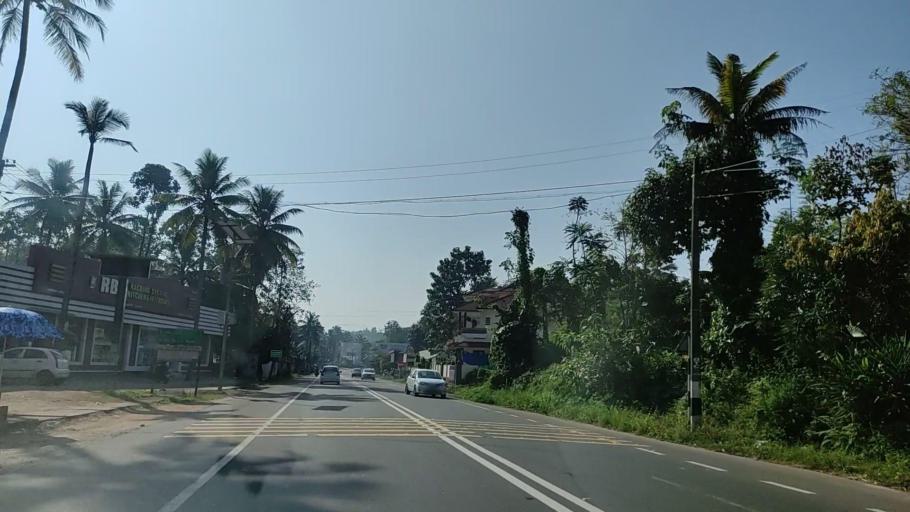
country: IN
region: Kerala
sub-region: Kollam
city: Punalur
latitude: 8.9282
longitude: 76.8541
